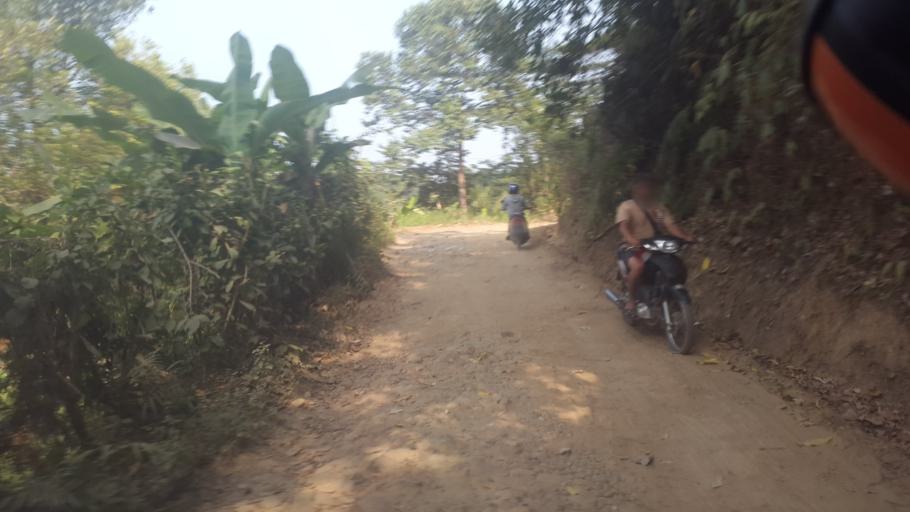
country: ID
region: West Java
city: Tugu
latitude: -6.9433
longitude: 106.4464
